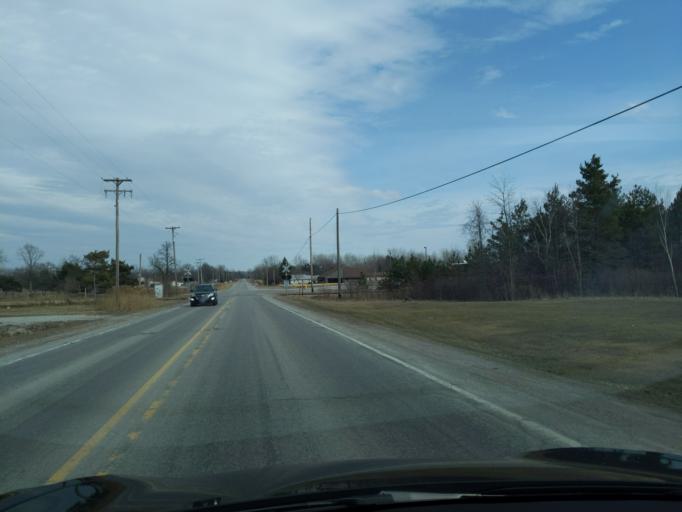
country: US
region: Michigan
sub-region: Bay County
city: Bay City
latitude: 43.6676
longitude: -83.9493
